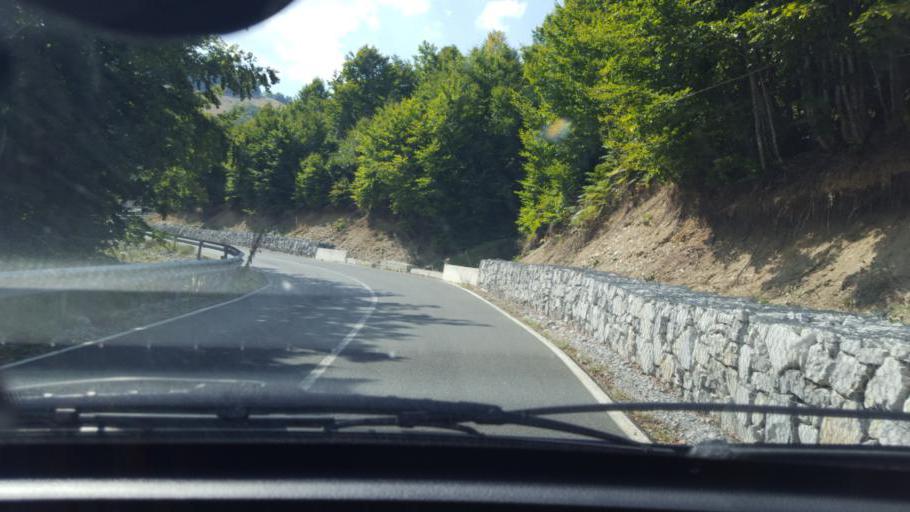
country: AL
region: Kukes
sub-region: Rrethi i Tropojes
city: Valbone
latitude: 42.5345
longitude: 19.7205
